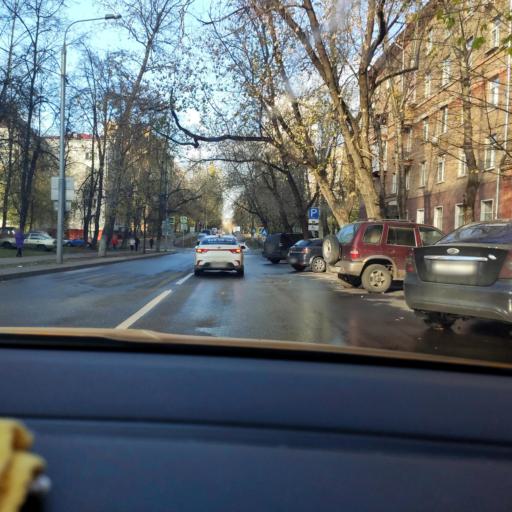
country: RU
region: Moscow
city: Tekstil'shchiki
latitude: 55.6963
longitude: 37.7436
